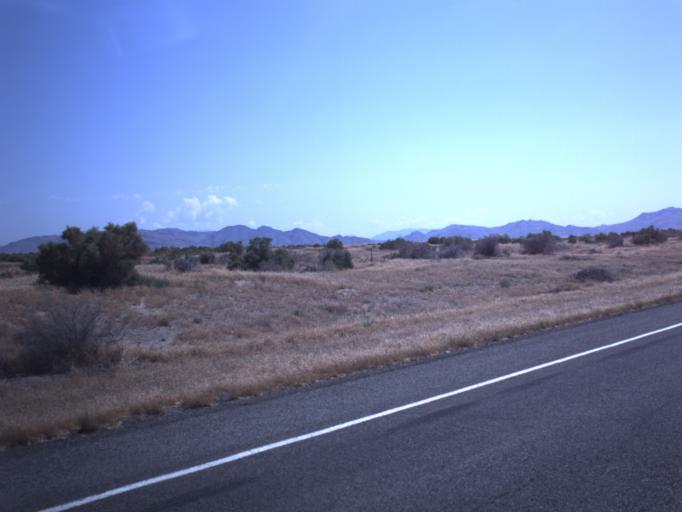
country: US
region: Utah
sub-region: Millard County
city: Delta
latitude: 39.4776
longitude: -112.4960
